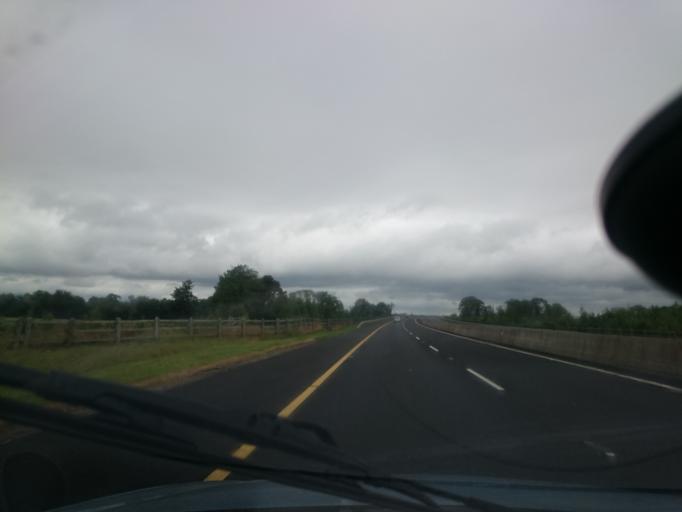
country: IE
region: Leinster
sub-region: Kildare
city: Castledermot
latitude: 52.9529
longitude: -6.8561
